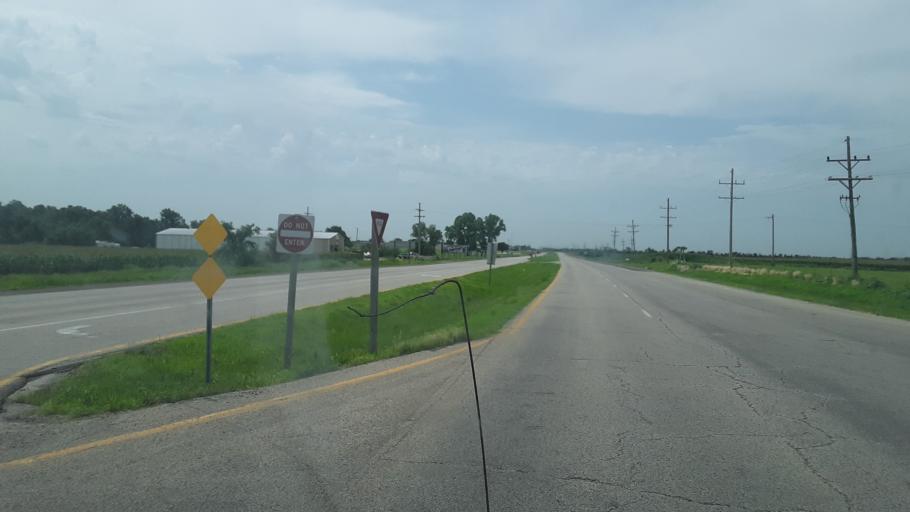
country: US
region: Kansas
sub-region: Reno County
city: South Hutchinson
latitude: 38.0078
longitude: -97.9405
